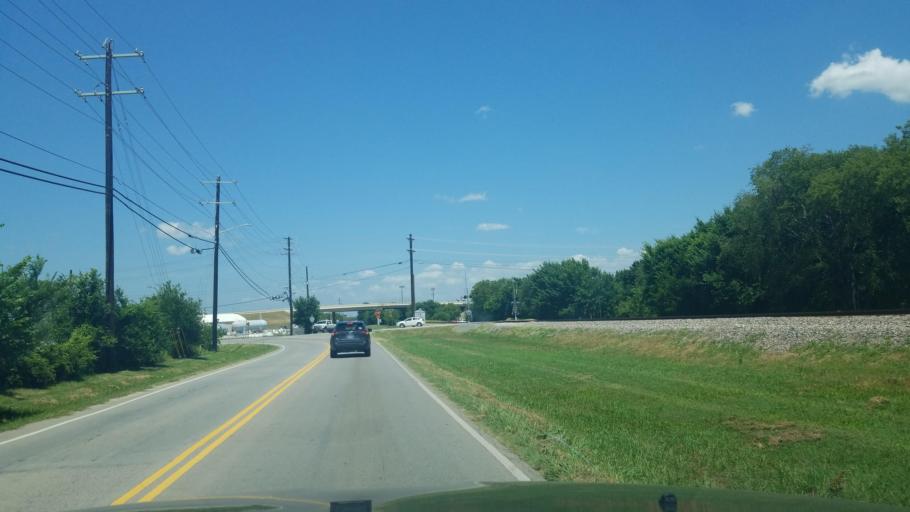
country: US
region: Texas
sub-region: Denton County
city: Denton
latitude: 33.2331
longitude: -97.1001
